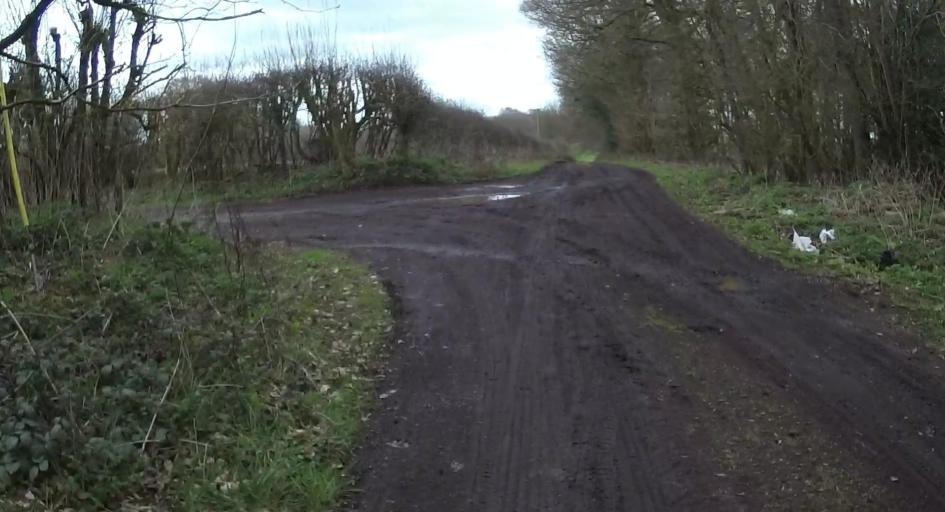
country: GB
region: England
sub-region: Hampshire
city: Old Basing
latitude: 51.1897
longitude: -1.0486
